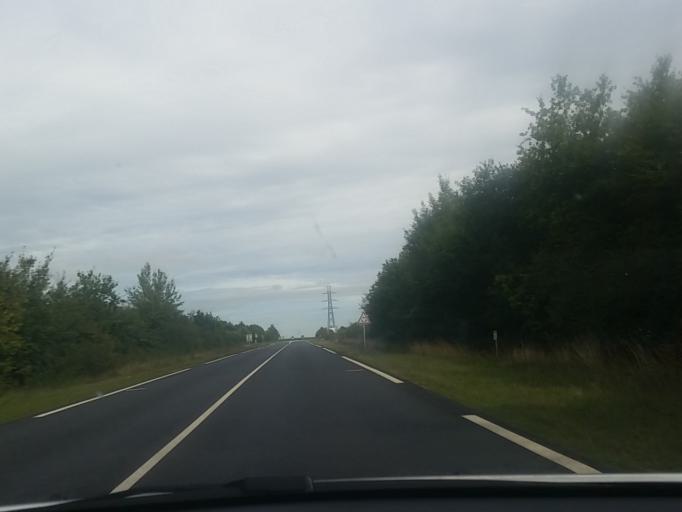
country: FR
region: Pays de la Loire
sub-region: Departement de la Loire-Atlantique
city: Chateaubriant
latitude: 47.7122
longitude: -1.3574
